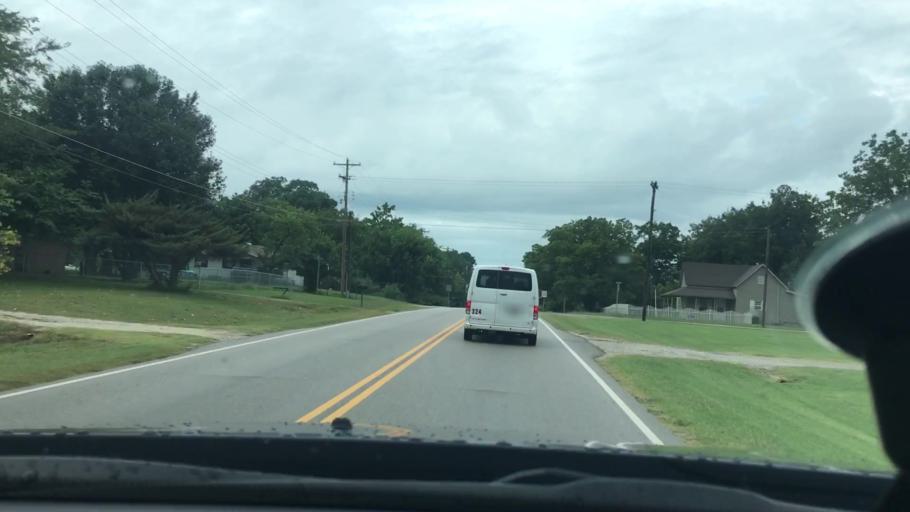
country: US
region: Oklahoma
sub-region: Murray County
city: Sulphur
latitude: 34.6274
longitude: -96.8352
